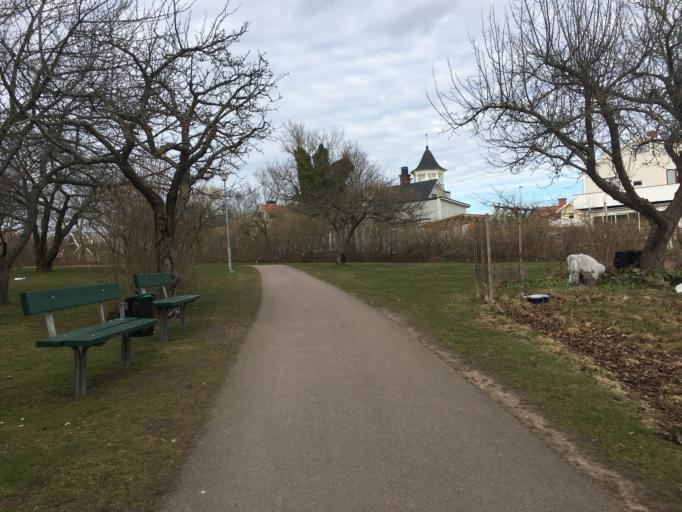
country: SE
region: Kalmar
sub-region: Kalmar Kommun
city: Kalmar
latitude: 56.6589
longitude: 16.3367
